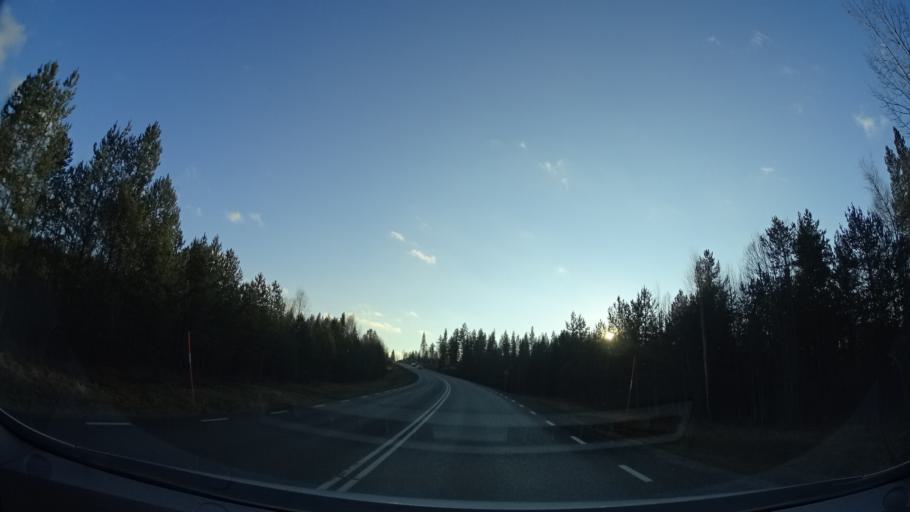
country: SE
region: Vaesterbotten
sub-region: Lycksele Kommun
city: Lycksele
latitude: 64.7483
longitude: 18.6693
